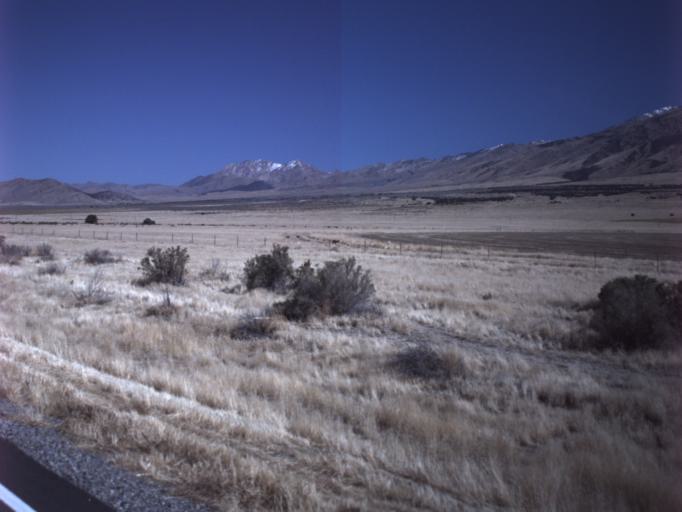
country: US
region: Utah
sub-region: Tooele County
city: Grantsville
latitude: 40.4638
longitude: -112.7470
